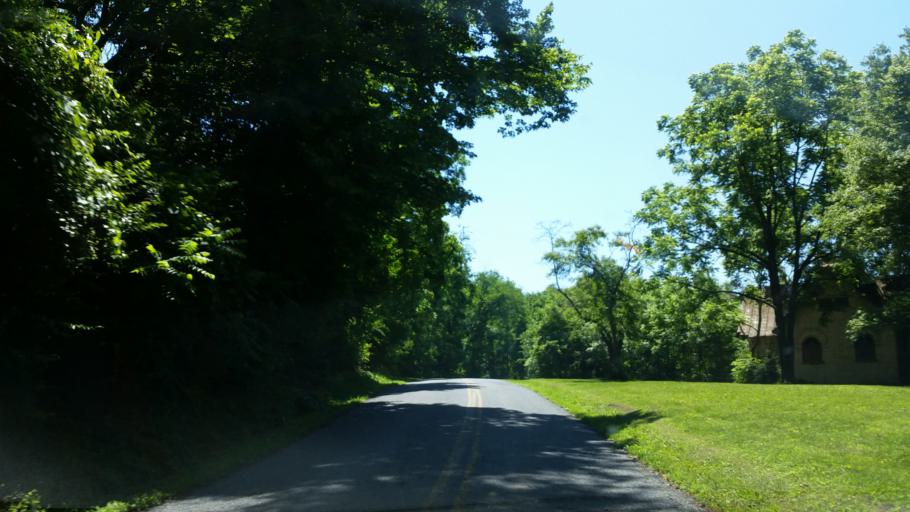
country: US
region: Pennsylvania
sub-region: Lebanon County
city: Fredericksburg
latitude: 40.4330
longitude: -76.4331
